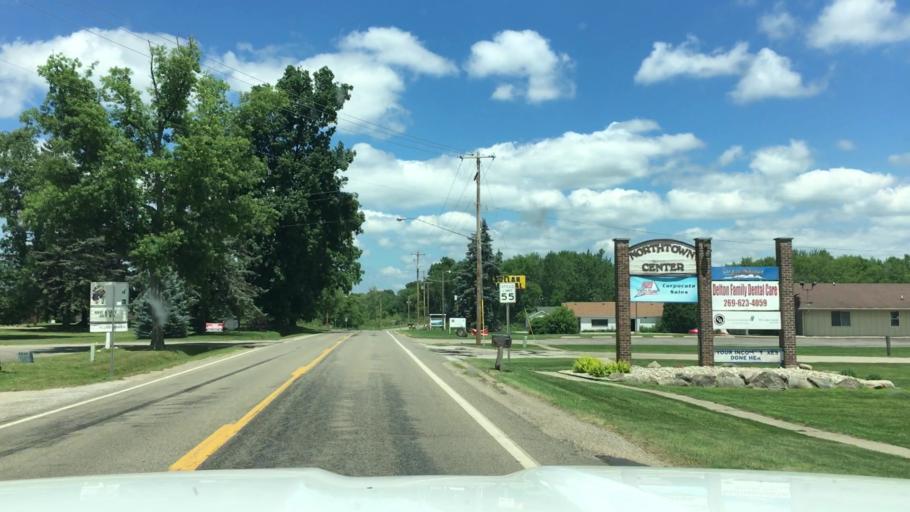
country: US
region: Michigan
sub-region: Barry County
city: Stony Point
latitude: 42.5062
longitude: -85.4089
